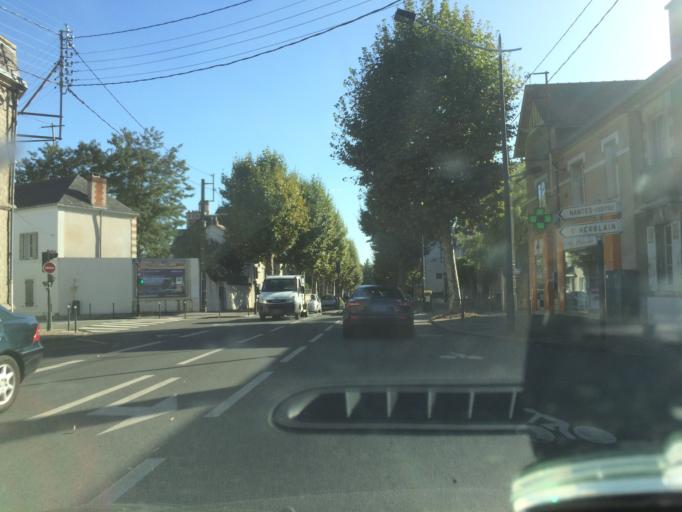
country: FR
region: Pays de la Loire
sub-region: Departement de la Loire-Atlantique
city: Nantes
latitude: 47.2365
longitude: -1.5634
